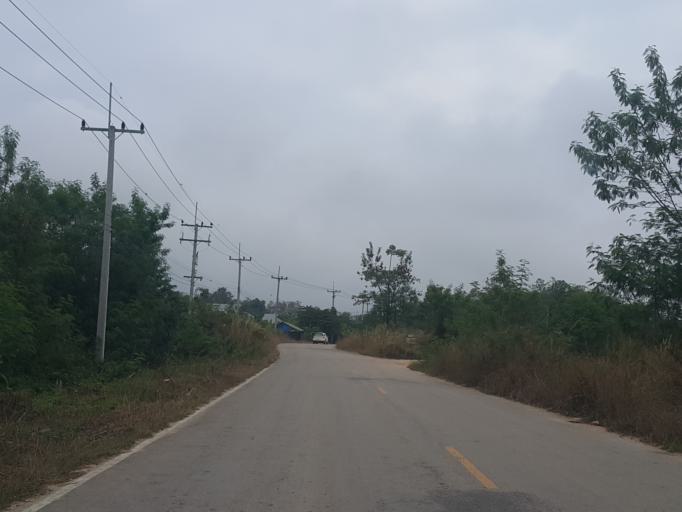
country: TH
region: Lampang
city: Lampang
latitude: 18.3298
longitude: 99.4868
